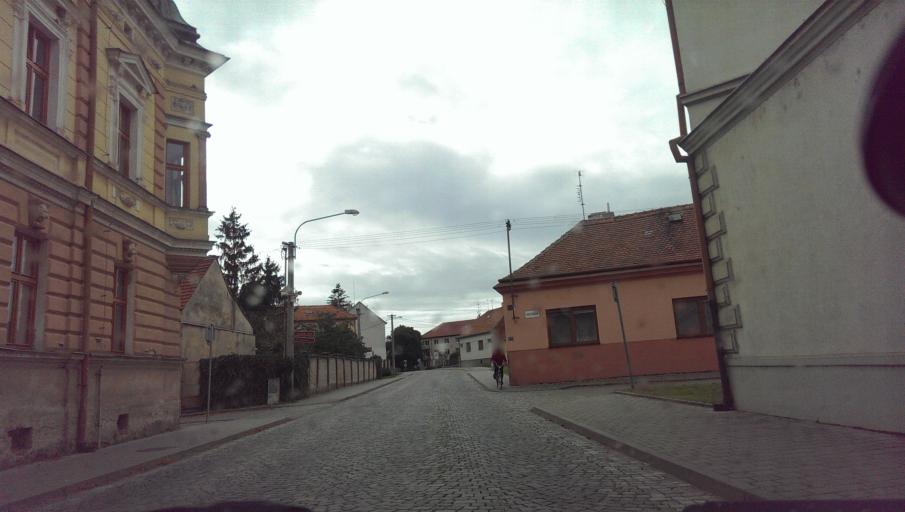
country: CZ
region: Zlin
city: Uhersky Ostroh
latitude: 48.9844
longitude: 17.3881
